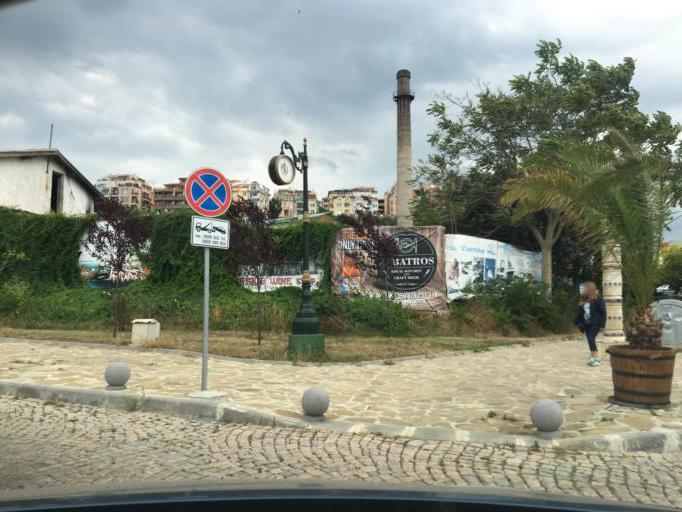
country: BG
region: Burgas
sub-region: Obshtina Sozopol
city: Sozopol
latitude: 42.4200
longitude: 27.6918
